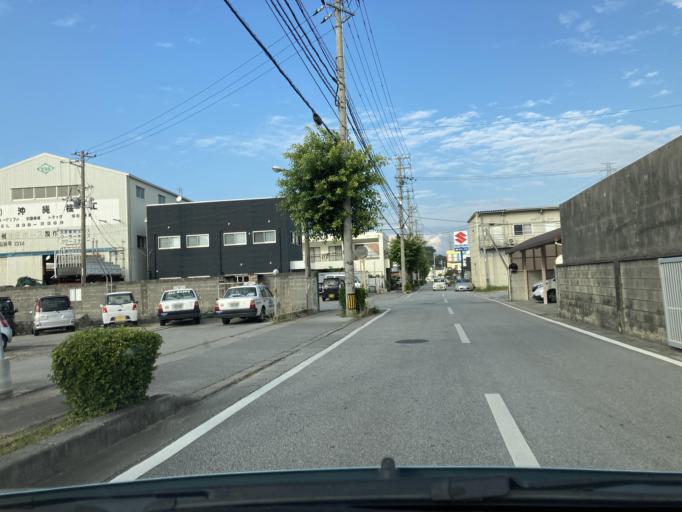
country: JP
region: Okinawa
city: Okinawa
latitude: 26.3566
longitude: 127.8070
